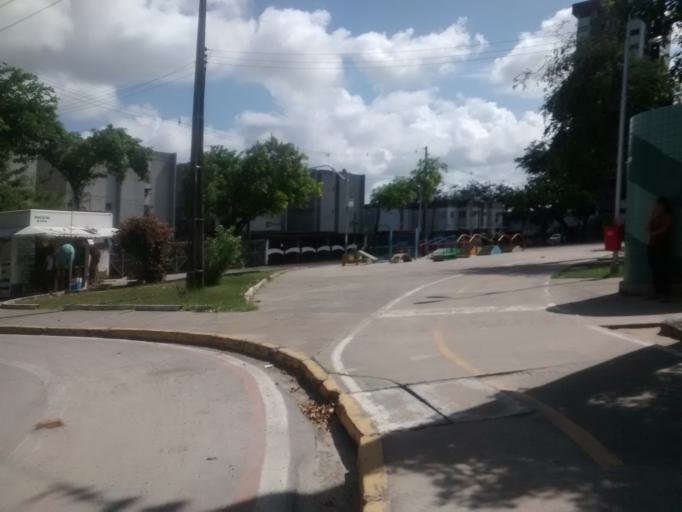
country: BR
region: Pernambuco
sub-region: Recife
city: Recife
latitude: -8.0965
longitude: -34.9146
